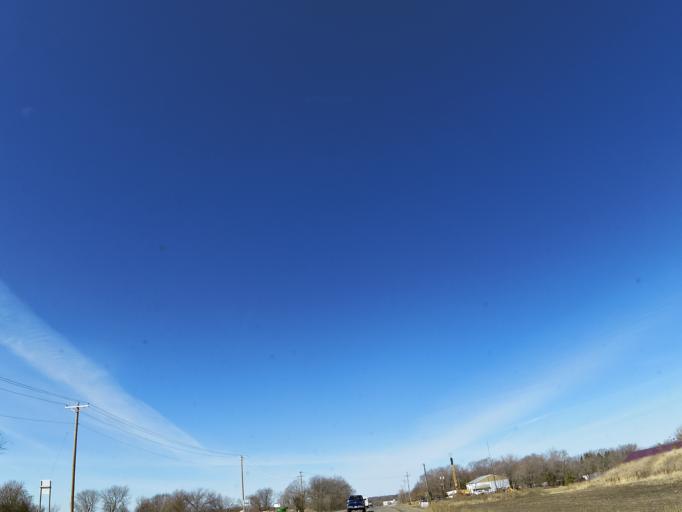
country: US
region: Minnesota
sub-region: Hennepin County
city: Greenfield
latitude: 45.0660
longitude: -93.6465
